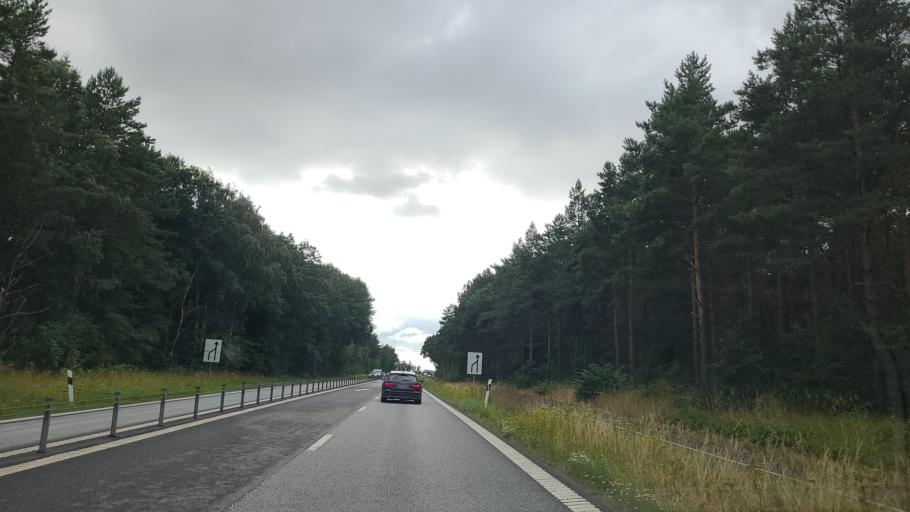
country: SE
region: Skane
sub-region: Kristianstads Kommun
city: Fjalkinge
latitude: 56.0408
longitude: 14.3077
